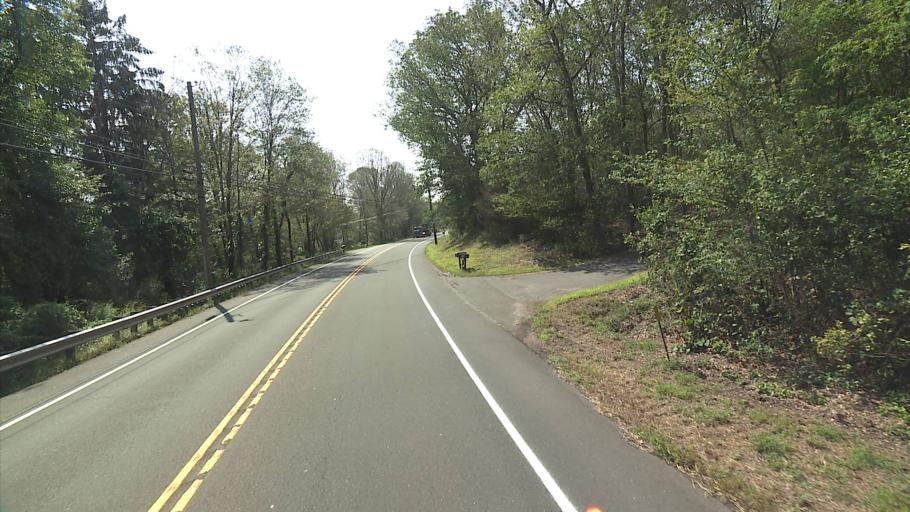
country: US
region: Connecticut
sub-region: Middlesex County
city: Durham
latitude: 41.4288
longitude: -72.6495
